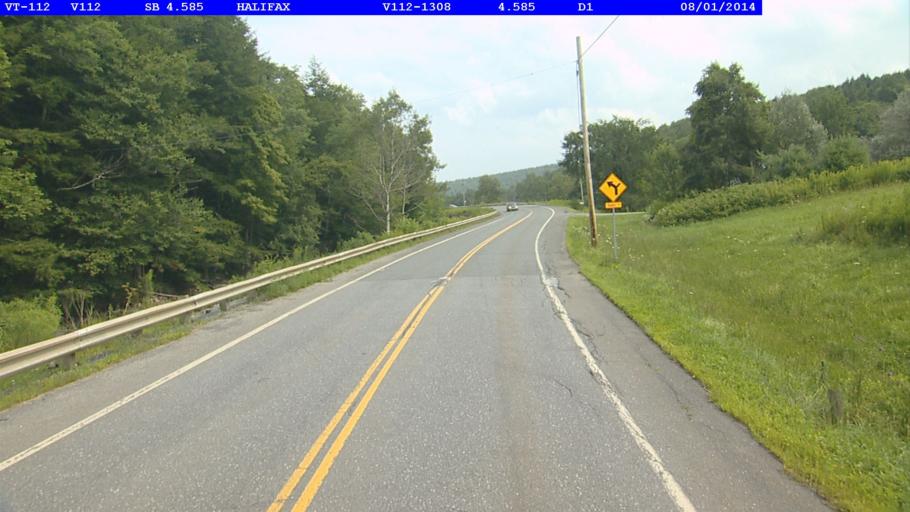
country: US
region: Massachusetts
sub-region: Franklin County
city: Colrain
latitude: 42.7648
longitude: -72.7916
